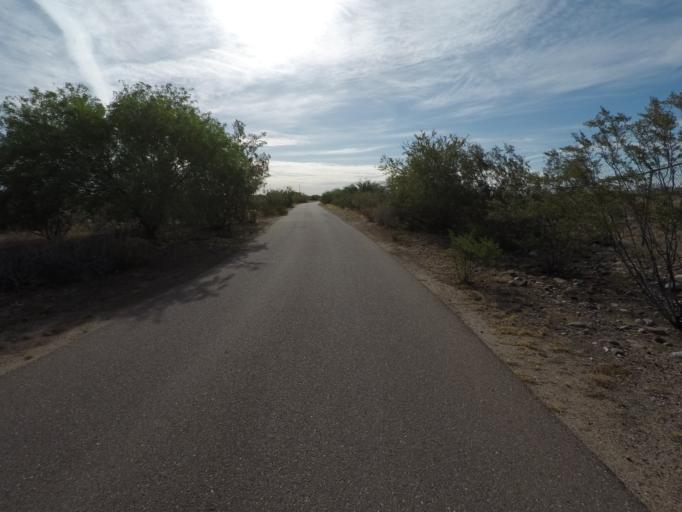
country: US
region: Arizona
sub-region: Maricopa County
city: Phoenix
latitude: 33.4198
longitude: -112.0608
